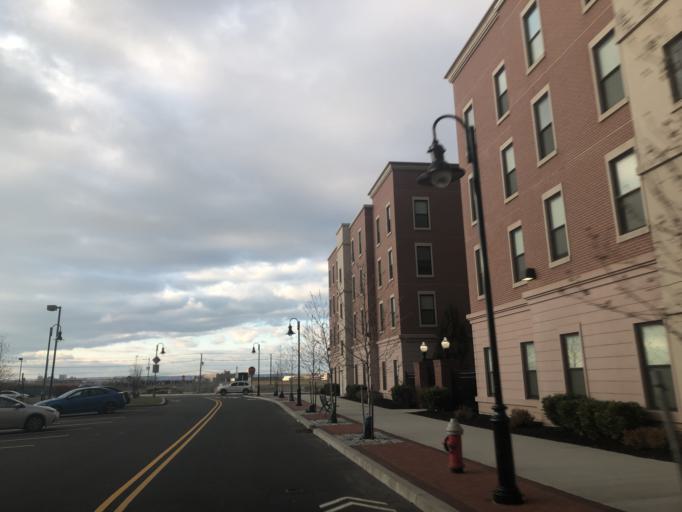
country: US
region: New Jersey
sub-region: Hudson County
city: Jersey City
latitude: 40.7118
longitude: -74.0958
